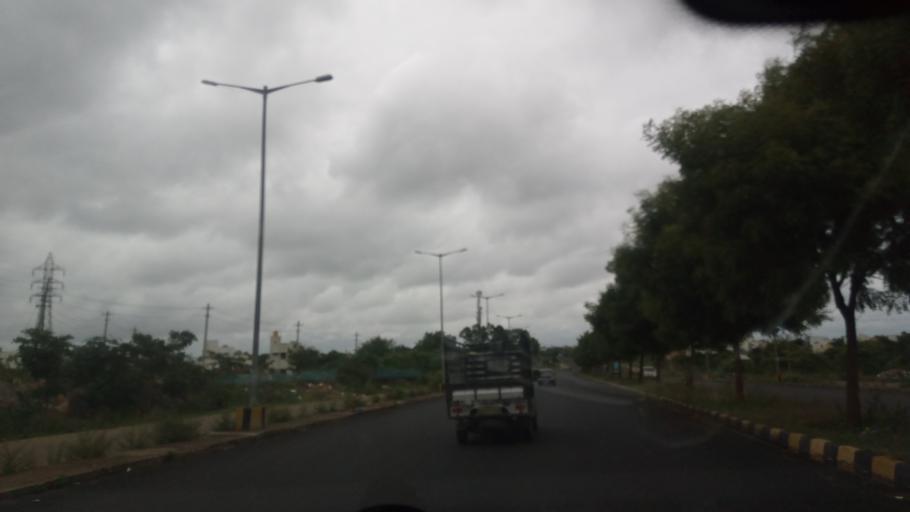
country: IN
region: Karnataka
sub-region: Mysore
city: Mysore
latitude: 12.3160
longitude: 76.5956
